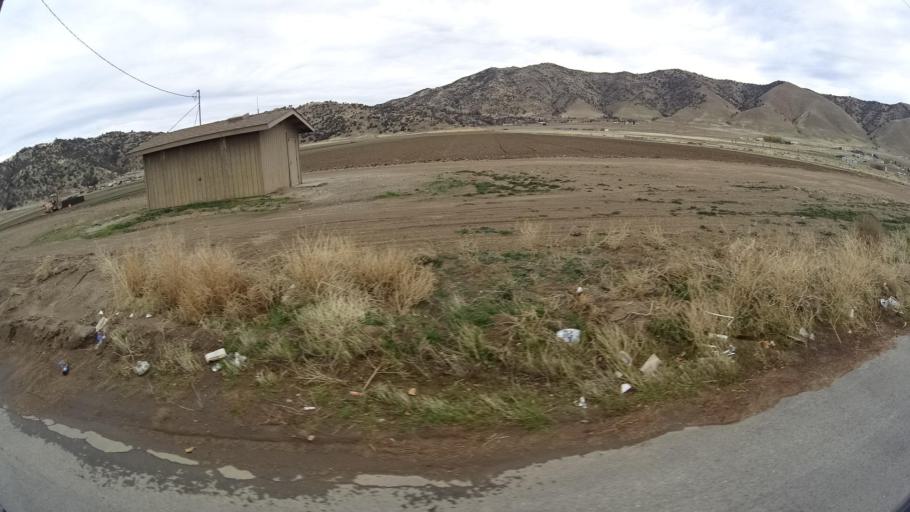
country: US
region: California
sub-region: Kern County
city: Bear Valley Springs
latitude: 35.1299
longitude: -118.5841
